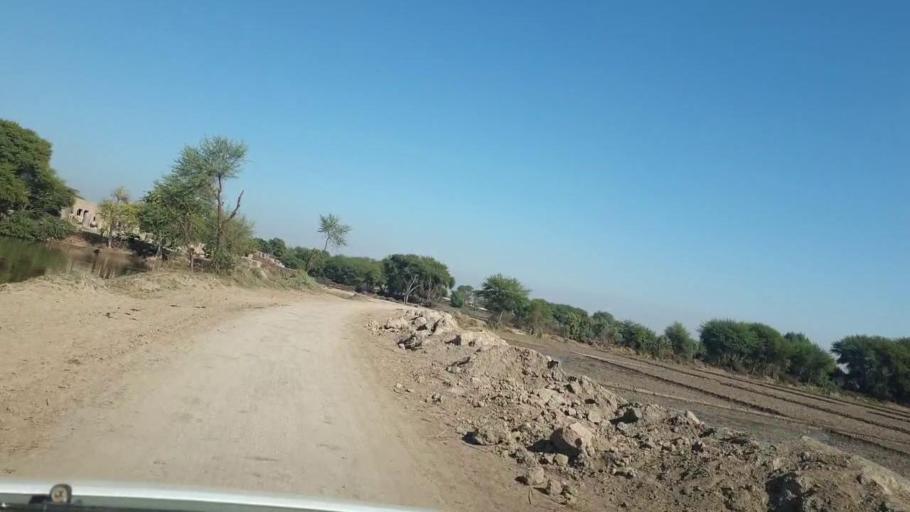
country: PK
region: Sindh
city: Dadu
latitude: 26.7959
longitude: 67.8310
